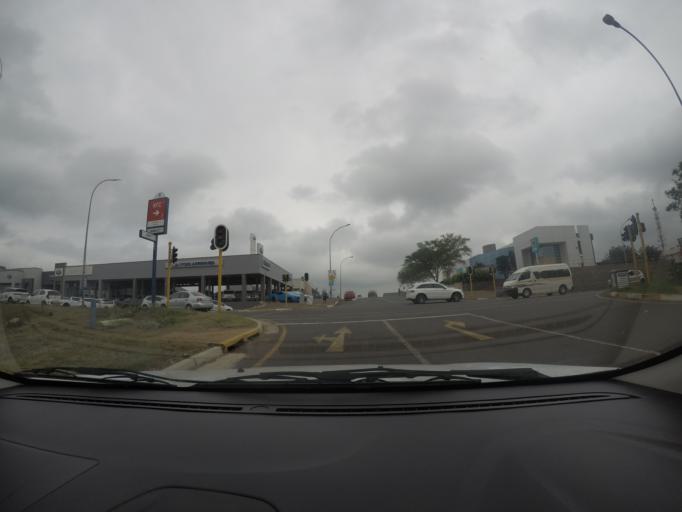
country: ZA
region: KwaZulu-Natal
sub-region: uThungulu District Municipality
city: Empangeni
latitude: -28.7404
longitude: 31.8925
